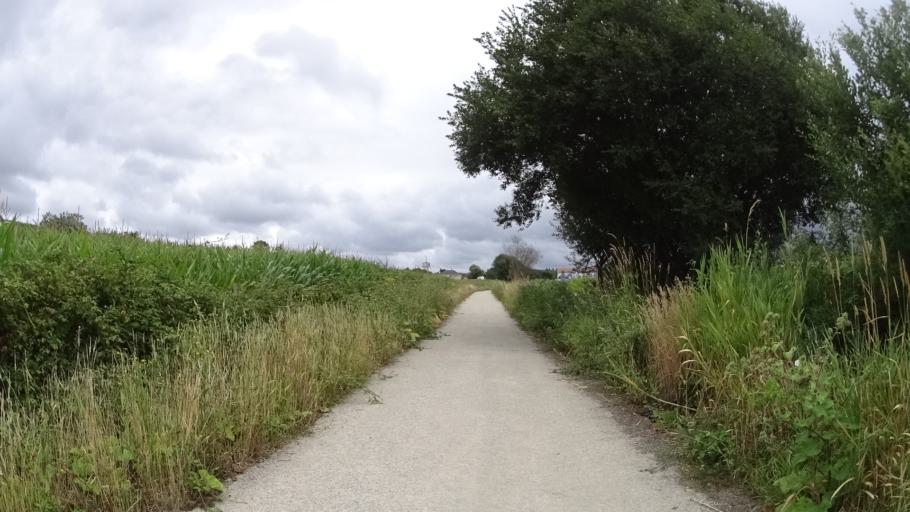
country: FR
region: Pays de la Loire
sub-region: Departement de la Loire-Atlantique
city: Saint-Jean-de-Boiseau
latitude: 47.1959
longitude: -1.7184
